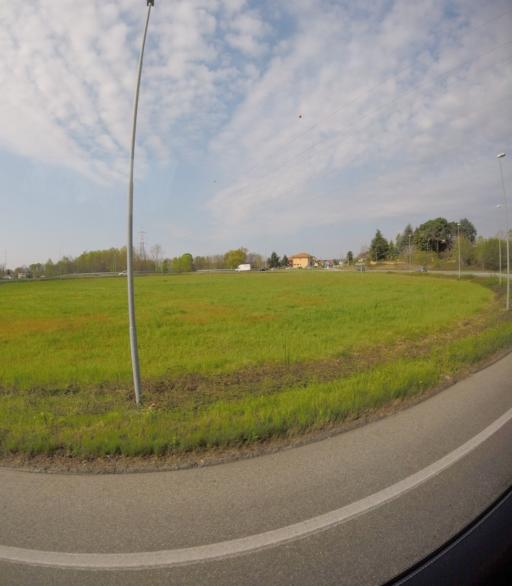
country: IT
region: Piedmont
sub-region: Provincia di Novara
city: Borgomanero
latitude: 45.7143
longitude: 8.4818
